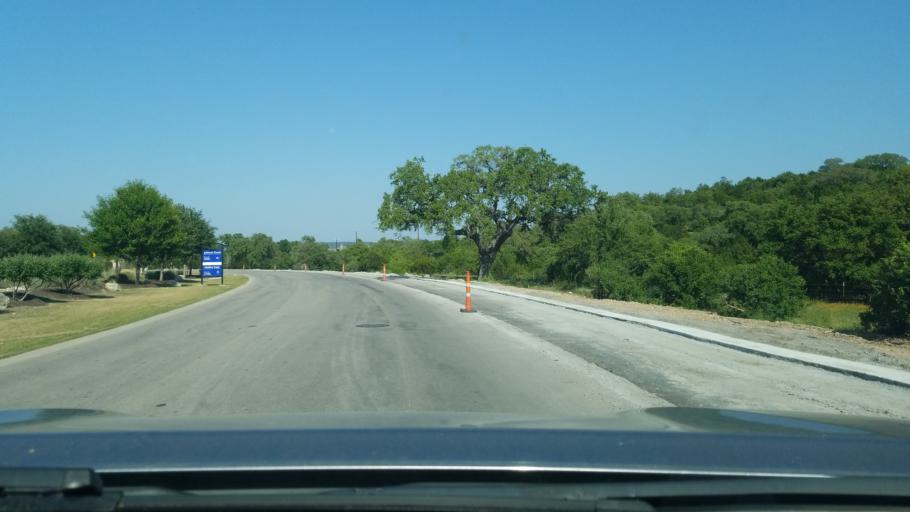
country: US
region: Texas
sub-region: Comal County
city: Bulverde
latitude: 29.7691
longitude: -98.4215
